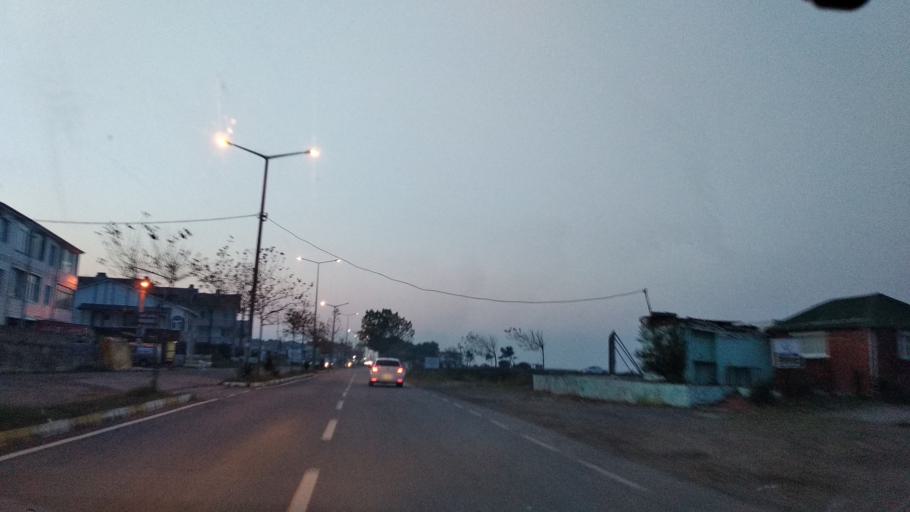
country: TR
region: Sakarya
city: Karasu
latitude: 41.0929
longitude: 30.7378
